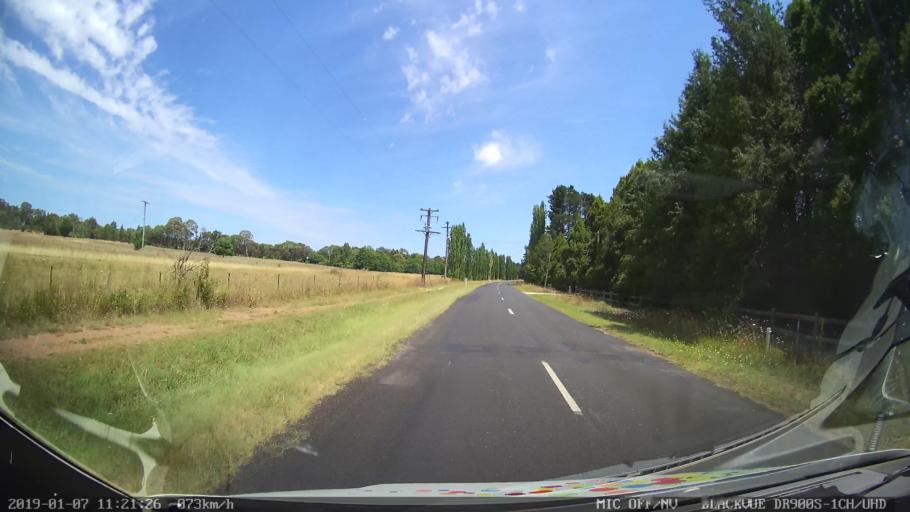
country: AU
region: New South Wales
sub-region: Armidale Dumaresq
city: Armidale
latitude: -30.4932
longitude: 151.6302
